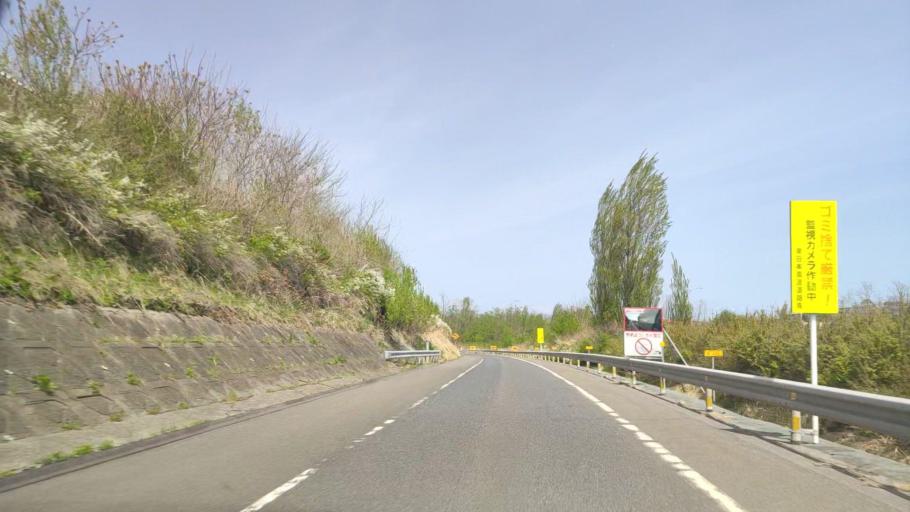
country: JP
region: Aomori
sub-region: Hachinohe Shi
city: Uchimaru
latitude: 40.4927
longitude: 141.4646
